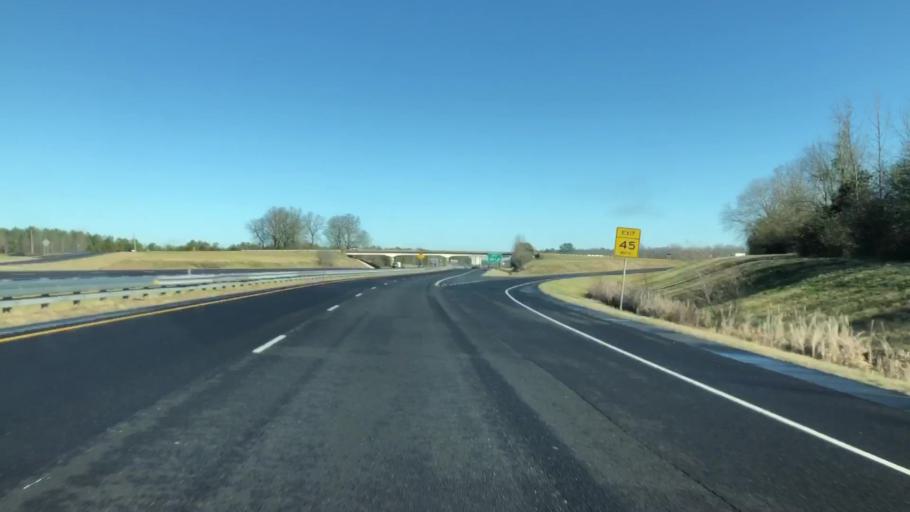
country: US
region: Alabama
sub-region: Limestone County
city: Ardmore
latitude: 34.9173
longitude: -86.9081
